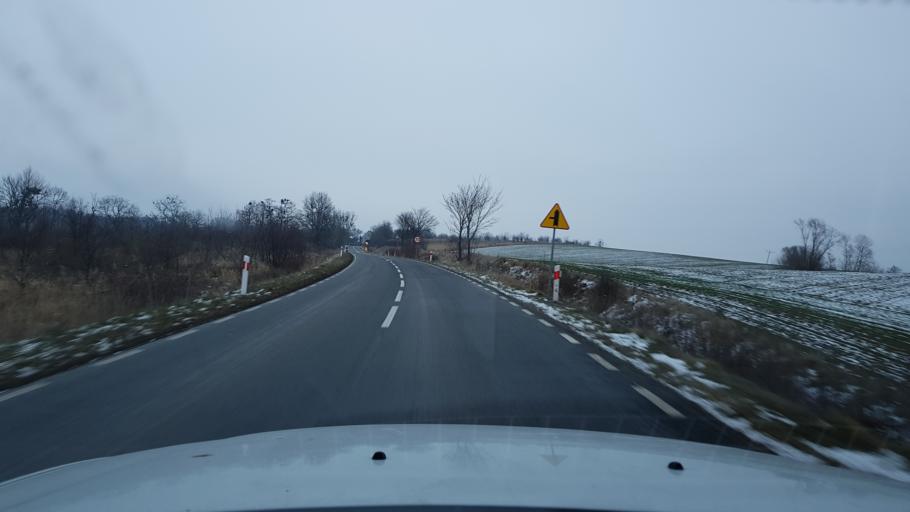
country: PL
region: West Pomeranian Voivodeship
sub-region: Powiat gryfinski
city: Cedynia
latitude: 52.8814
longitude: 14.2781
